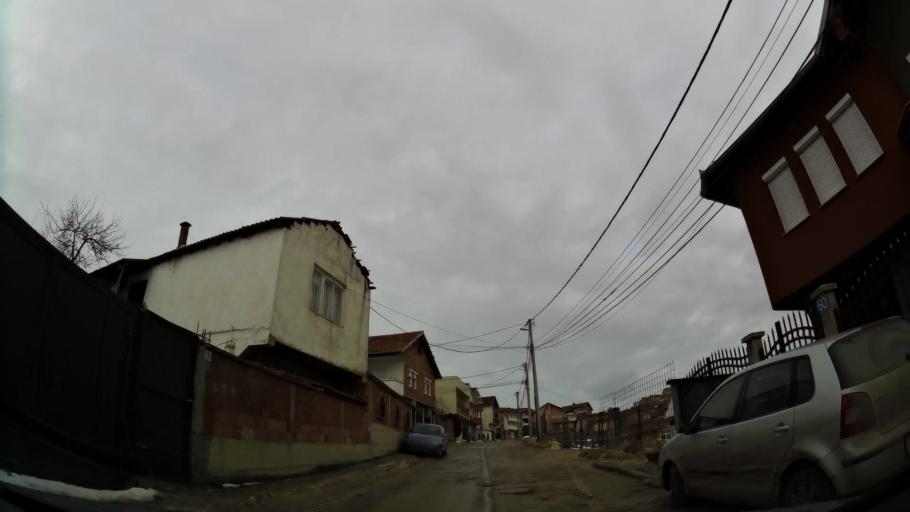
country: XK
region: Pristina
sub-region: Komuna e Prishtines
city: Pristina
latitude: 42.6853
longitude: 21.1737
